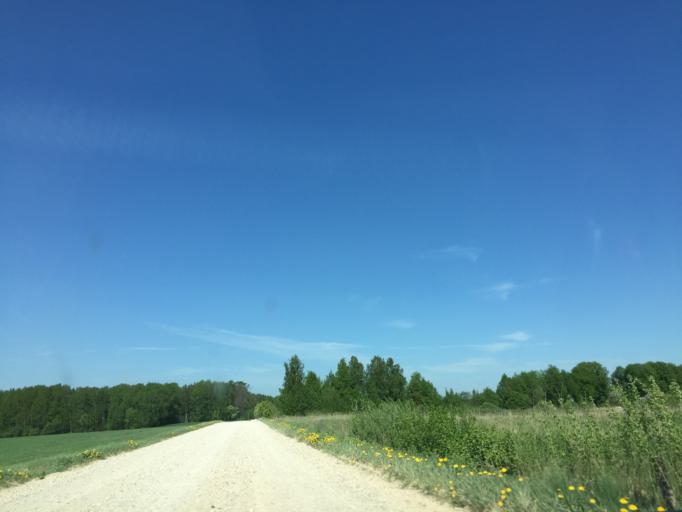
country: LV
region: Ikskile
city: Ikskile
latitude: 56.8728
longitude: 24.4996
